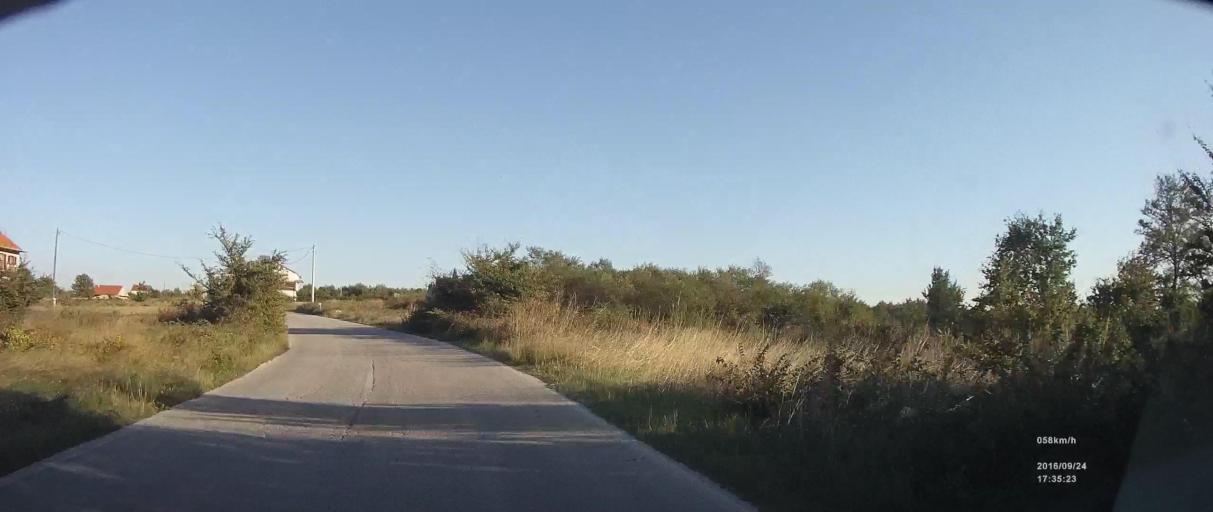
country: HR
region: Zadarska
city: Posedarje
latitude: 44.1605
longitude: 15.4664
